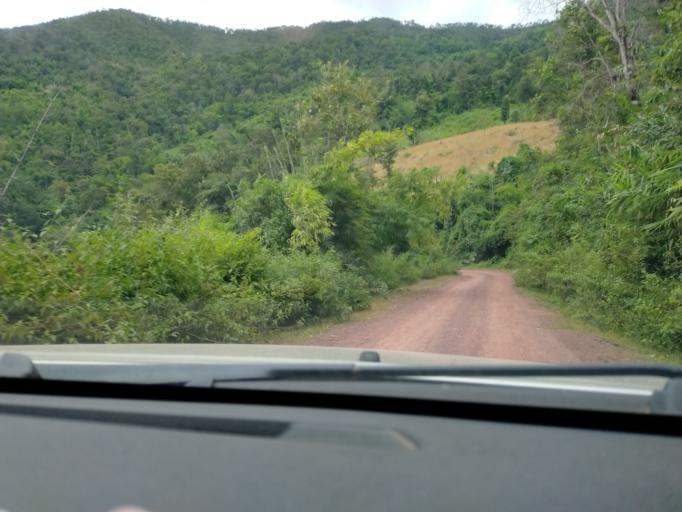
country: TH
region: Nan
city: Chaloem Phra Kiat
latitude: 19.7842
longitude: 101.3597
